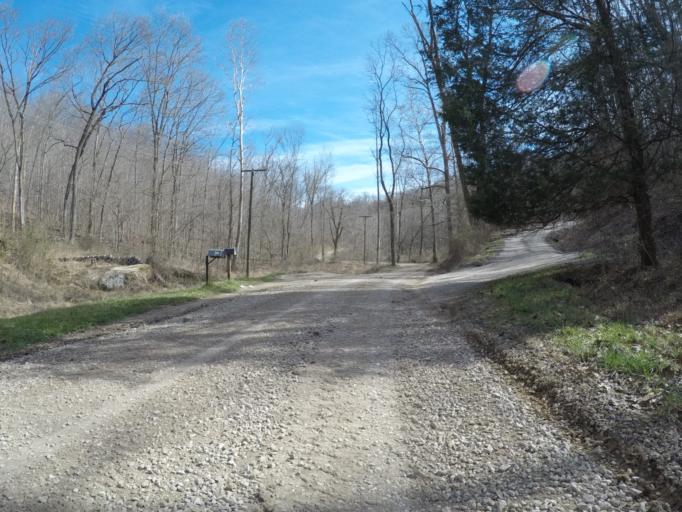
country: US
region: West Virginia
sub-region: Wayne County
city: Ceredo
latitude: 38.3432
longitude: -82.5408
